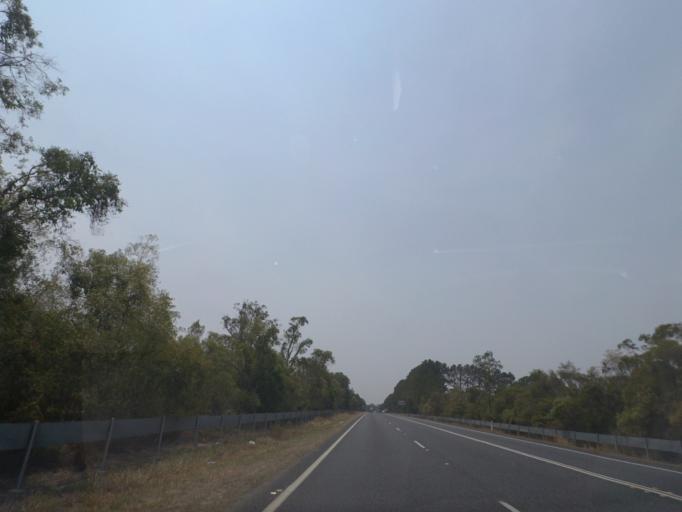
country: AU
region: New South Wales
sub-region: Ballina
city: Ballina
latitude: -28.9427
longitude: 153.4687
